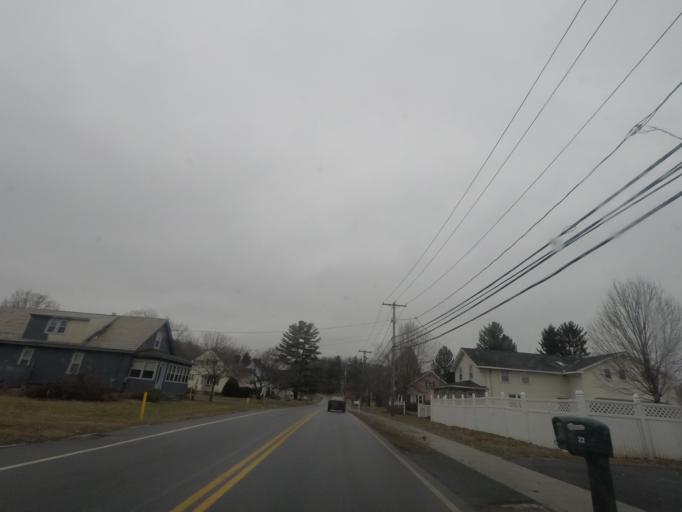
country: US
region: New York
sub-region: Saratoga County
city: Mechanicville
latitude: 42.9007
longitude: -73.6980
